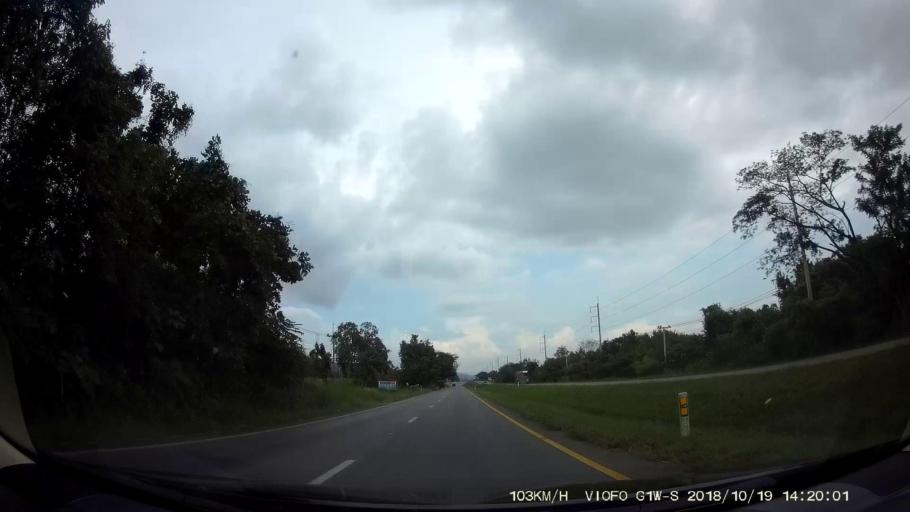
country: TH
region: Chaiyaphum
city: Kaeng Khro
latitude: 16.0353
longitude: 102.2516
